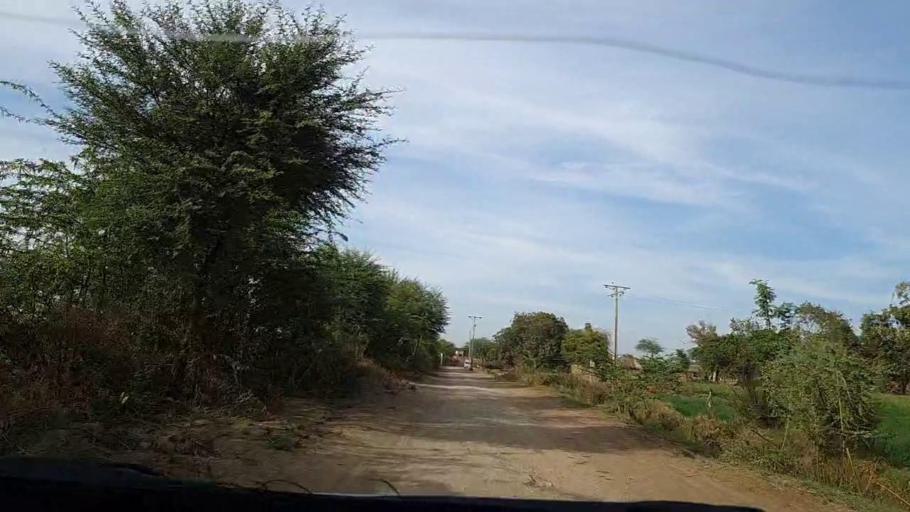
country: PK
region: Sindh
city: Dhoro Naro
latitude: 25.4484
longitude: 69.5126
